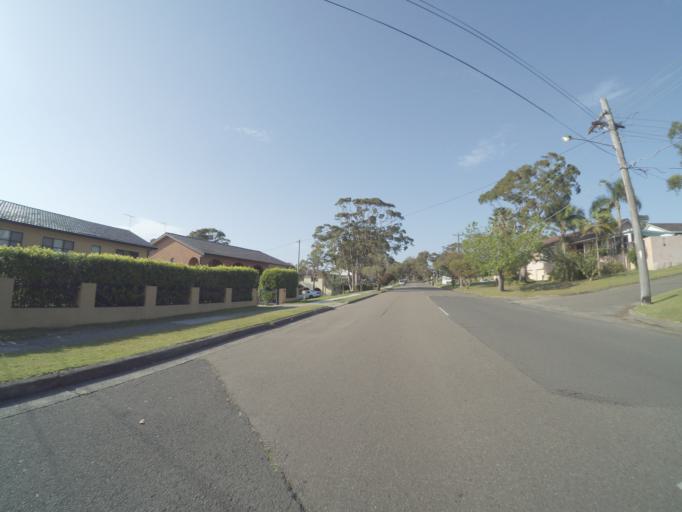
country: AU
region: New South Wales
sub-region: Sutherland Shire
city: Dolans Bay
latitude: -34.0692
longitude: 151.1379
